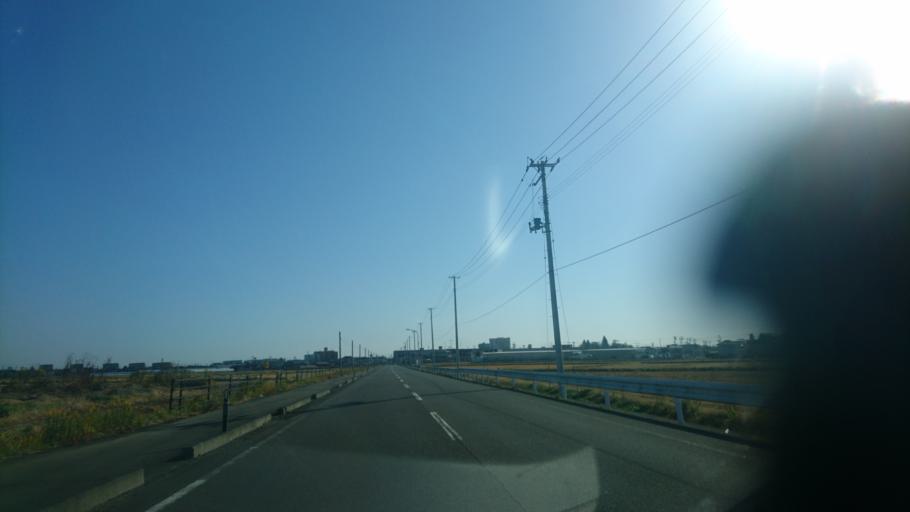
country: JP
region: Miyagi
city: Iwanuma
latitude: 38.1221
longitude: 140.8588
